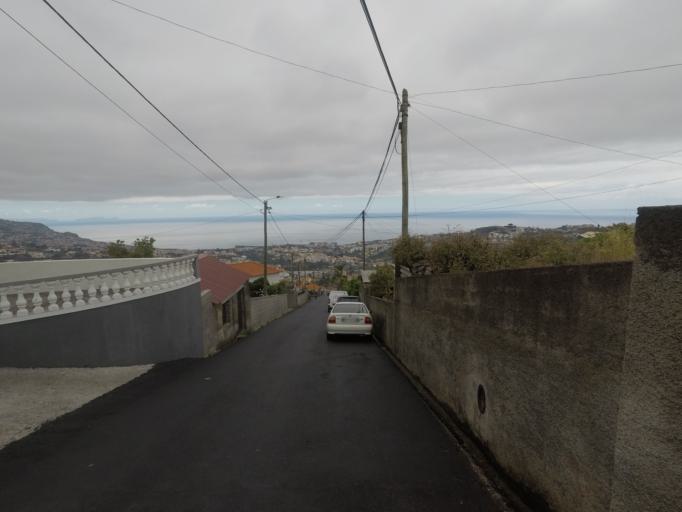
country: PT
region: Madeira
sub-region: Funchal
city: Nossa Senhora do Monte
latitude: 32.6735
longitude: -16.9388
